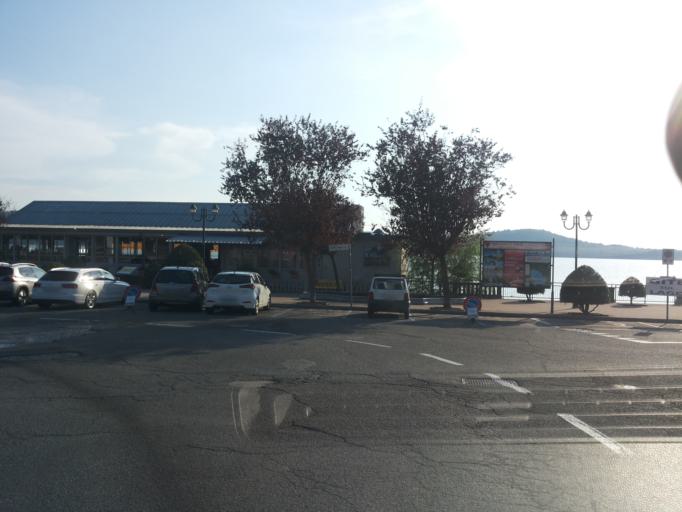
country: IT
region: Piedmont
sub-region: Provincia di Biella
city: Viverone
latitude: 45.4207
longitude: 8.0471
